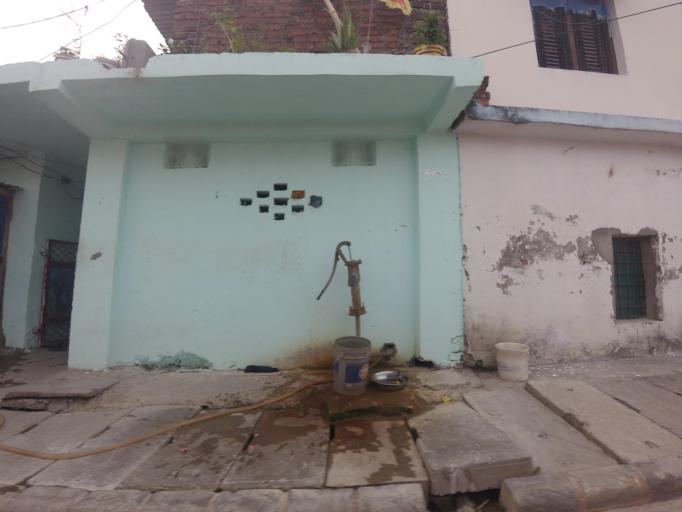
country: NP
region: Western Region
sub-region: Lumbini Zone
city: Bhairahawa
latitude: 27.5088
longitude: 83.4239
